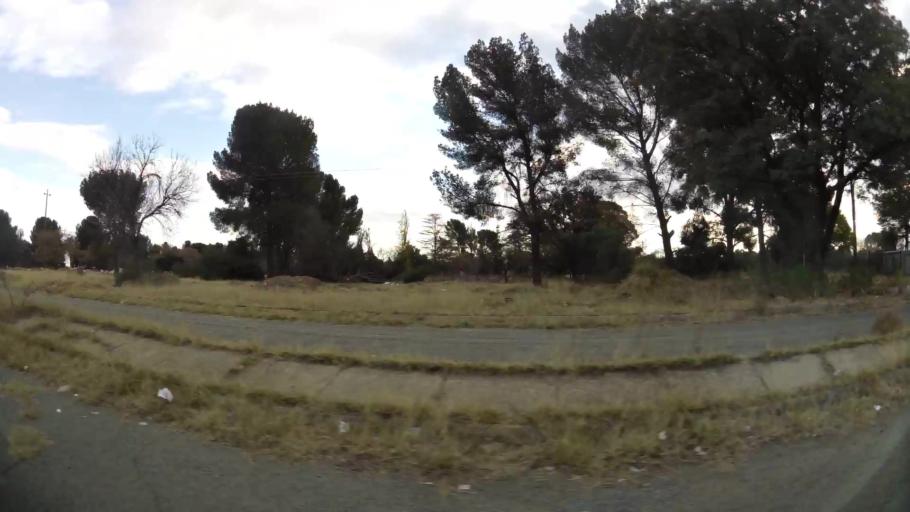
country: ZA
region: Orange Free State
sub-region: Lejweleputswa District Municipality
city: Welkom
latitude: -27.9976
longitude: 26.7188
